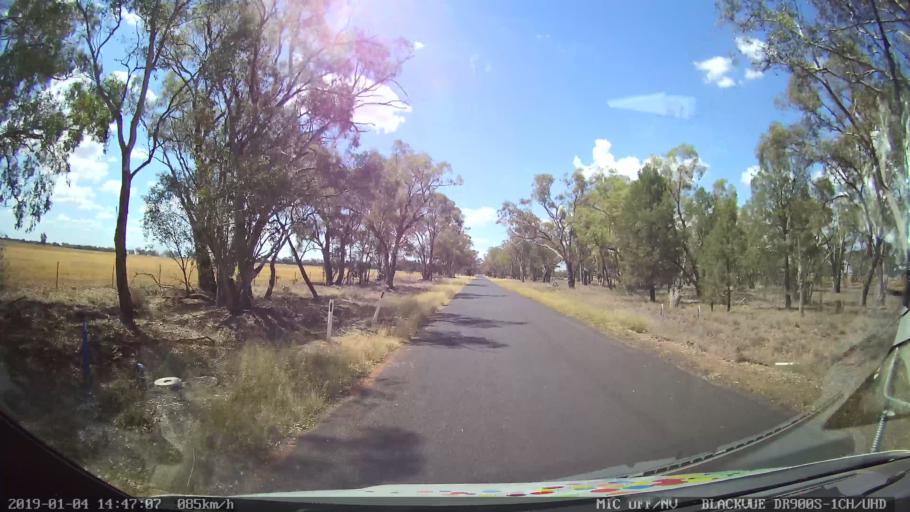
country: AU
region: New South Wales
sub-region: Dubbo Municipality
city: Dubbo
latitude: -32.0729
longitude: 148.6596
